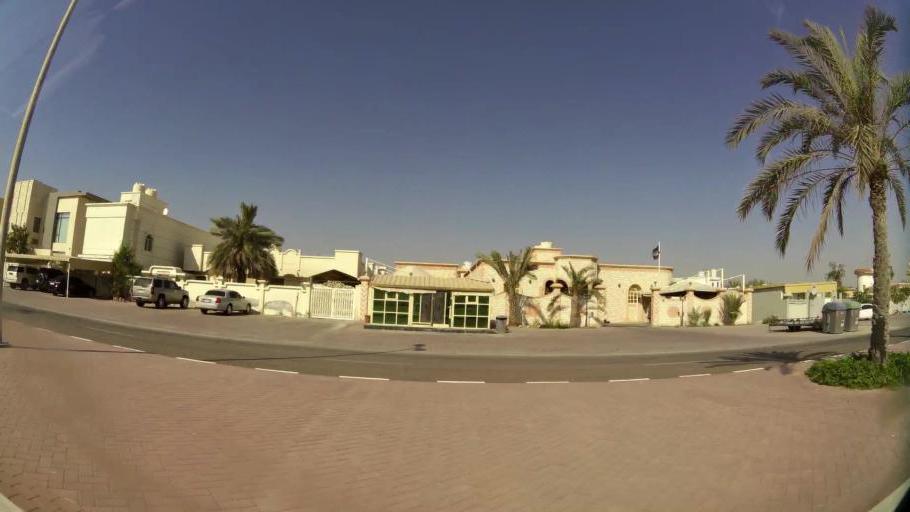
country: AE
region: Ajman
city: Ajman
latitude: 25.4169
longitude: 55.4656
